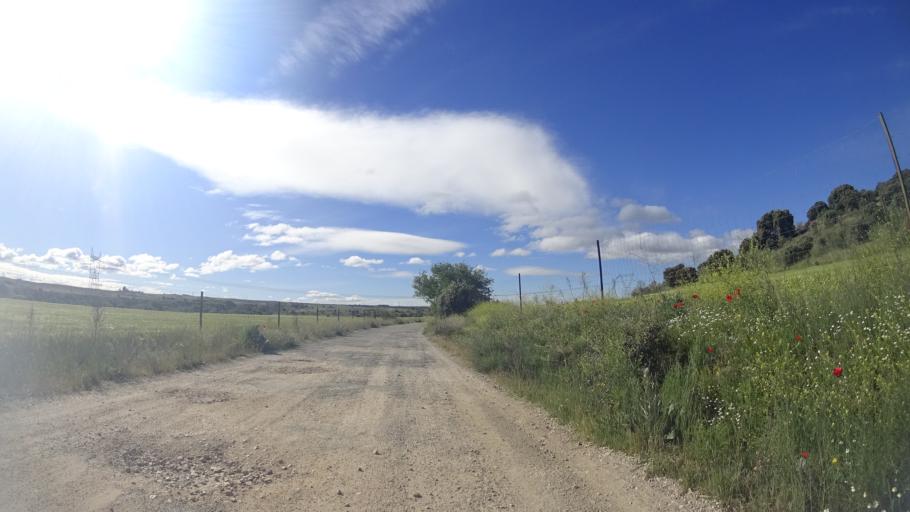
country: ES
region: Madrid
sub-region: Provincia de Madrid
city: Villanueva del Pardillo
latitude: 40.5053
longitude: -3.9399
